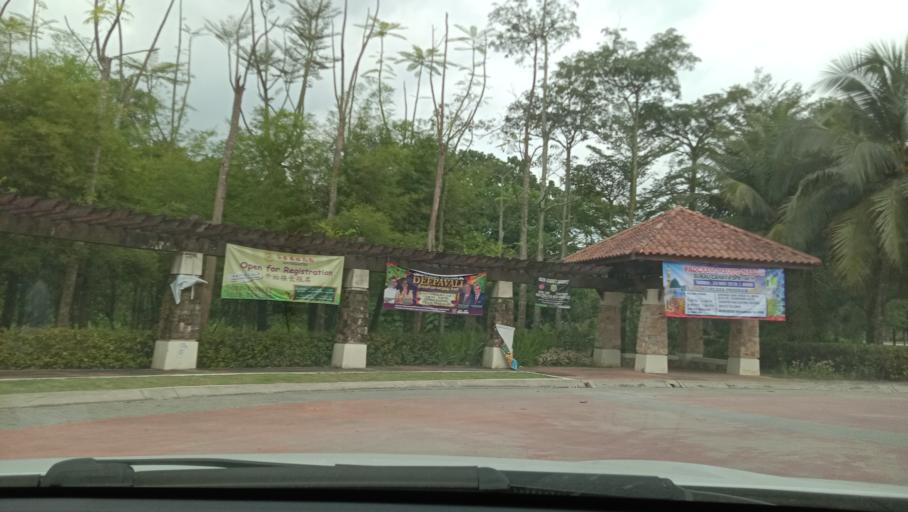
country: MY
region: Selangor
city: Kampung Baru Subang
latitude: 3.1357
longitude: 101.5019
